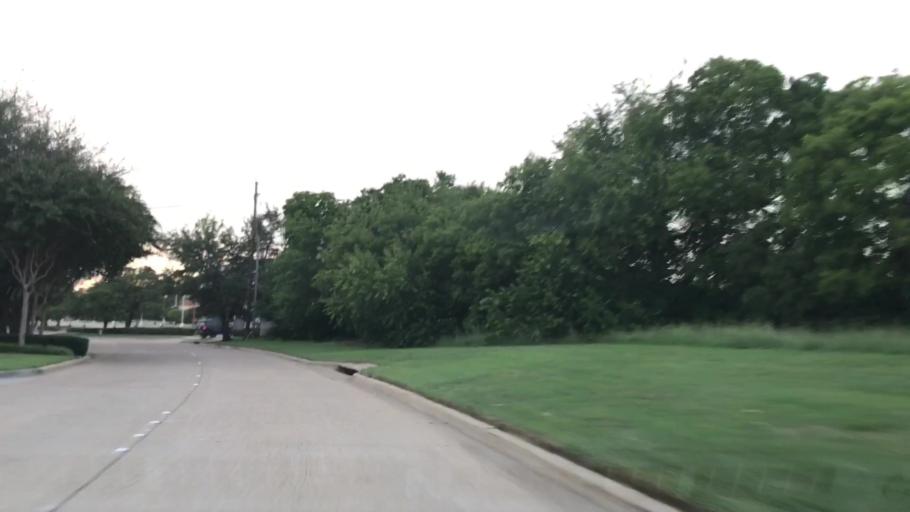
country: US
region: Texas
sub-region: Dallas County
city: Addison
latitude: 33.0188
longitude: -96.8385
